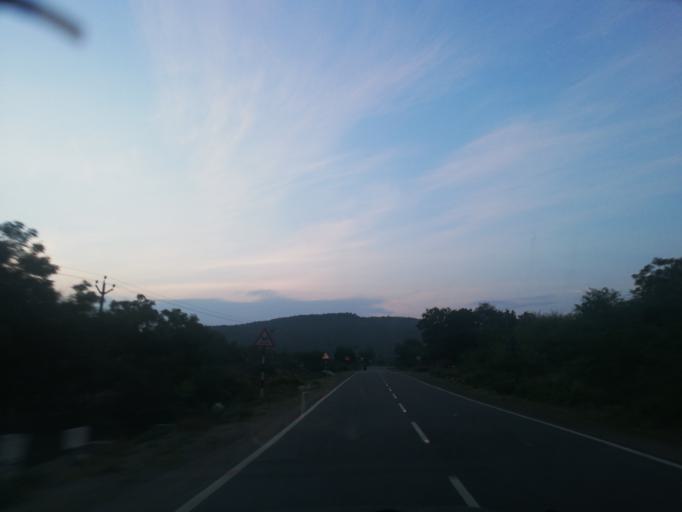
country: IN
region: Andhra Pradesh
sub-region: Guntur
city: Macherla
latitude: 16.6664
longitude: 79.2835
